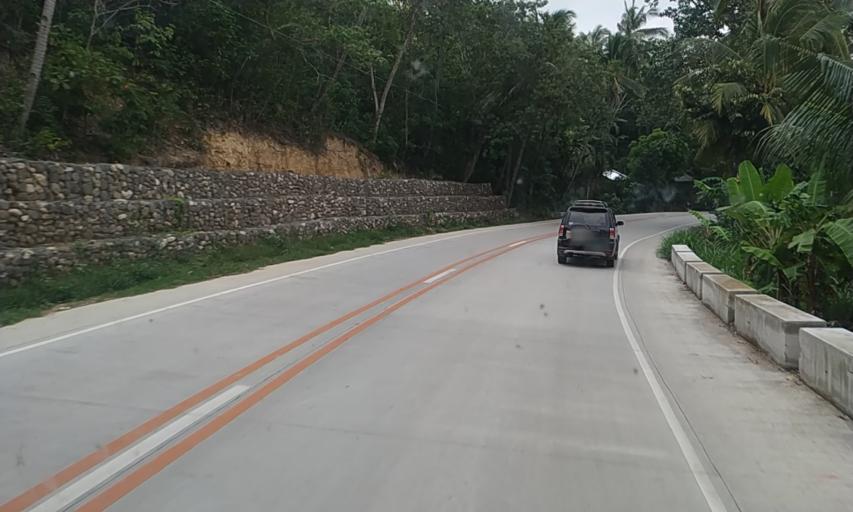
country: PH
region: Central Visayas
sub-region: Province of Negros Oriental
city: Basak
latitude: 10.2055
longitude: 123.3001
